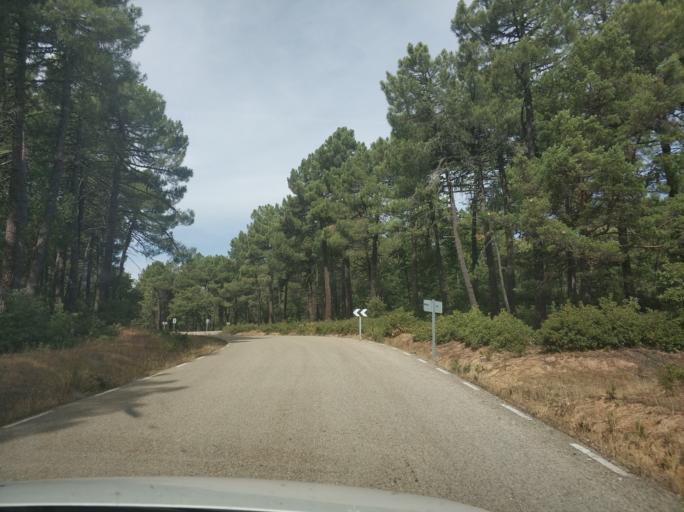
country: ES
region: Castille and Leon
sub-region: Provincia de Soria
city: Duruelo de la Sierra
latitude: 41.8914
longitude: -2.9435
